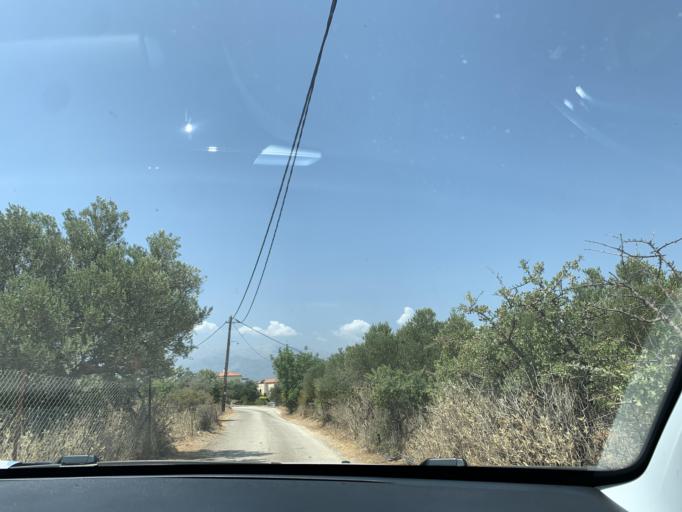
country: GR
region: Crete
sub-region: Nomos Chanias
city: Kalivai
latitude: 35.4526
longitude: 24.2334
